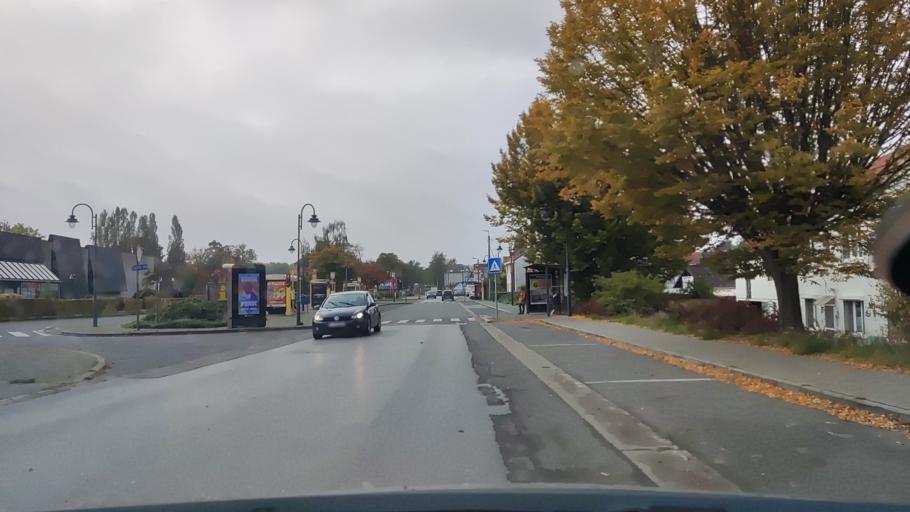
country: BE
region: Wallonia
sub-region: Province du Brabant Wallon
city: Jodoigne
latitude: 50.7238
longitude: 4.8774
